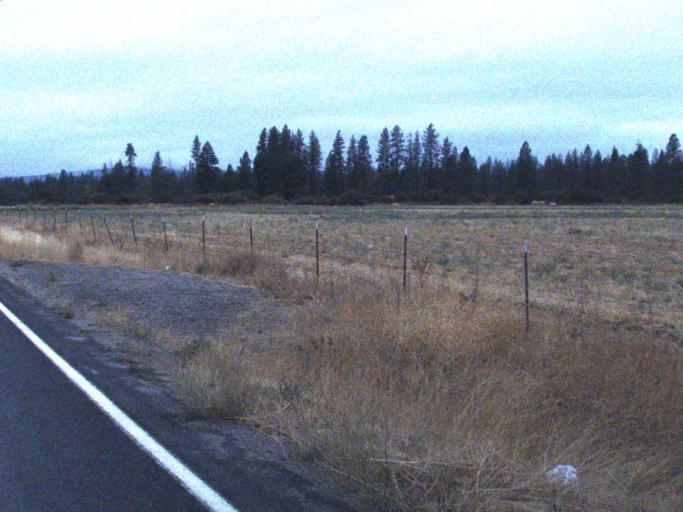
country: US
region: Washington
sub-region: Spokane County
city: Deer Park
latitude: 47.9143
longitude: -117.7993
